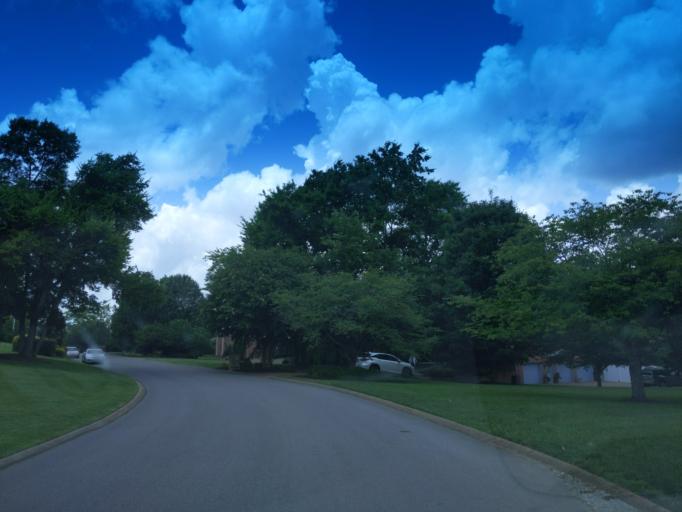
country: US
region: Tennessee
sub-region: Williamson County
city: Brentwood Estates
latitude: 36.0236
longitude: -86.7803
